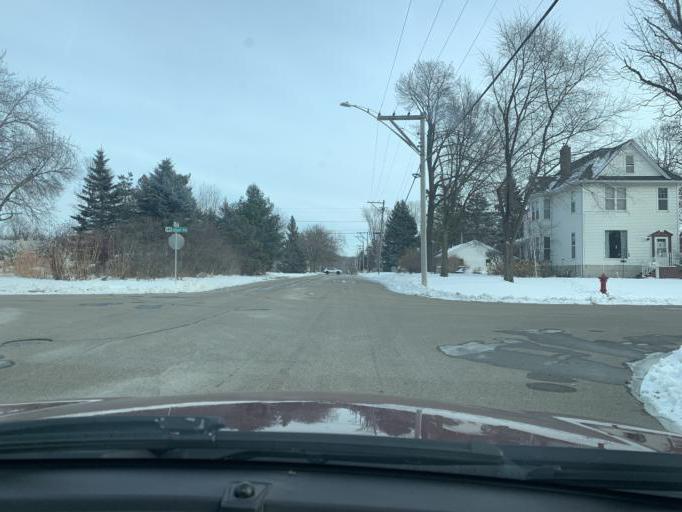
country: US
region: Minnesota
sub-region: Washington County
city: Saint Paul Park
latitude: 44.8385
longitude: -92.9873
